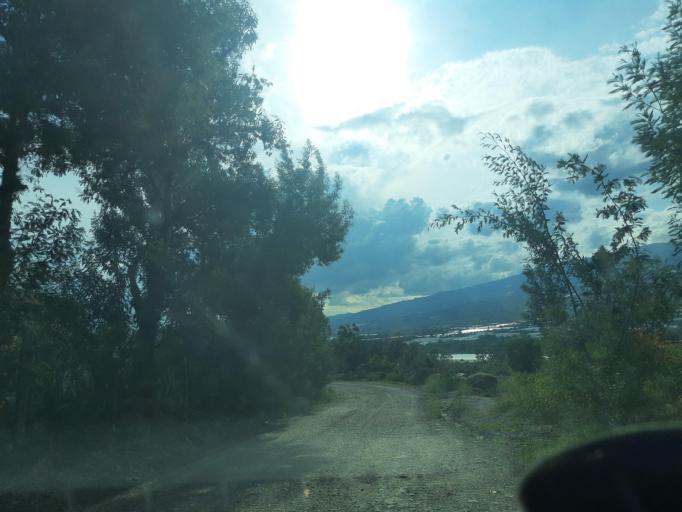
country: CO
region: Boyaca
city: Villa de Leiva
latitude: 5.6656
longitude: -73.5682
